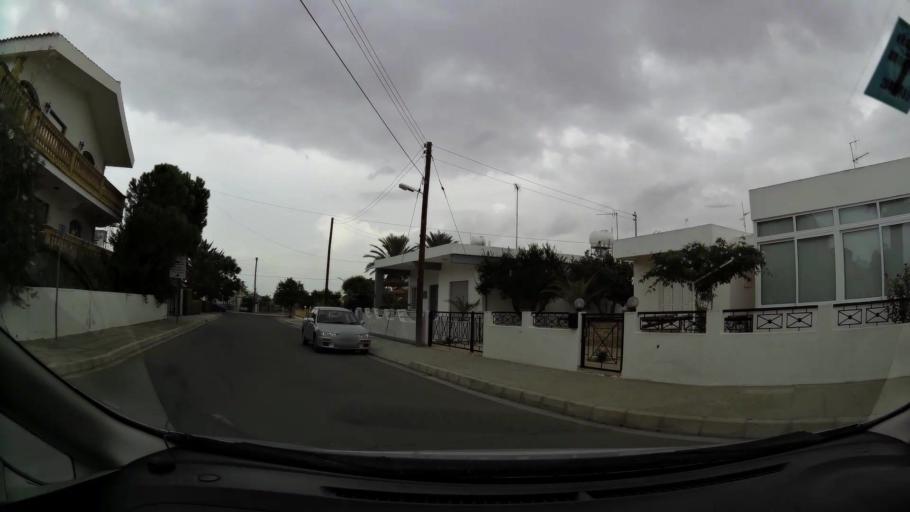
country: CY
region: Lefkosia
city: Geri
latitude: 35.1010
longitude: 33.3813
